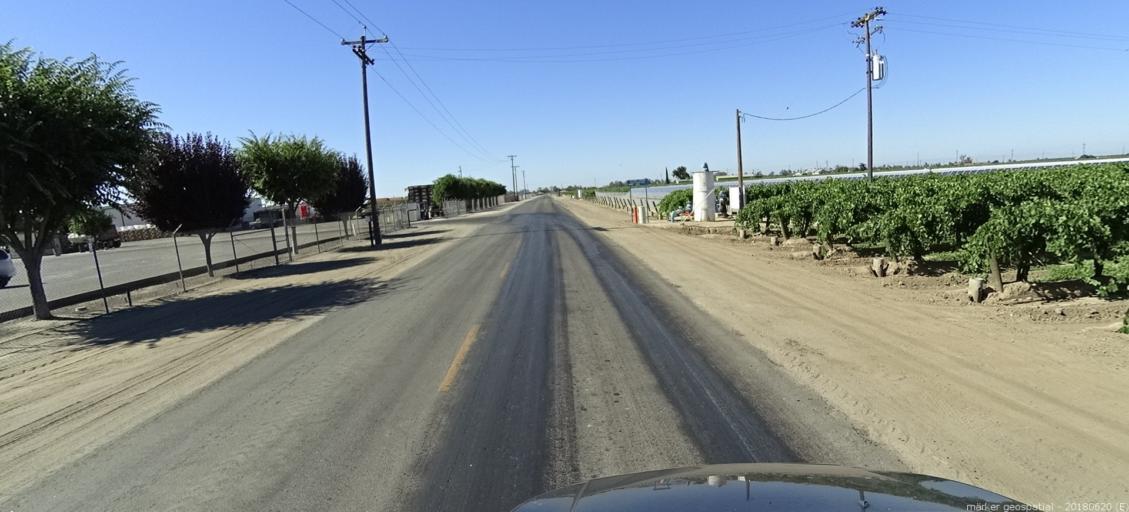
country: US
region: California
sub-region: Madera County
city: Parkwood
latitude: 36.9215
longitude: -120.0466
